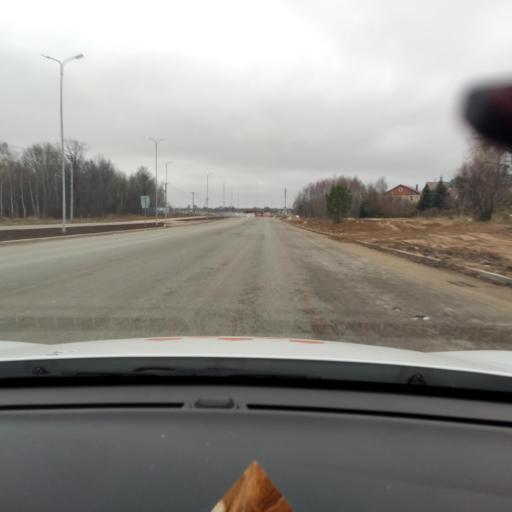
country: RU
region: Tatarstan
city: Osinovo
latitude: 55.8534
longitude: 48.9073
